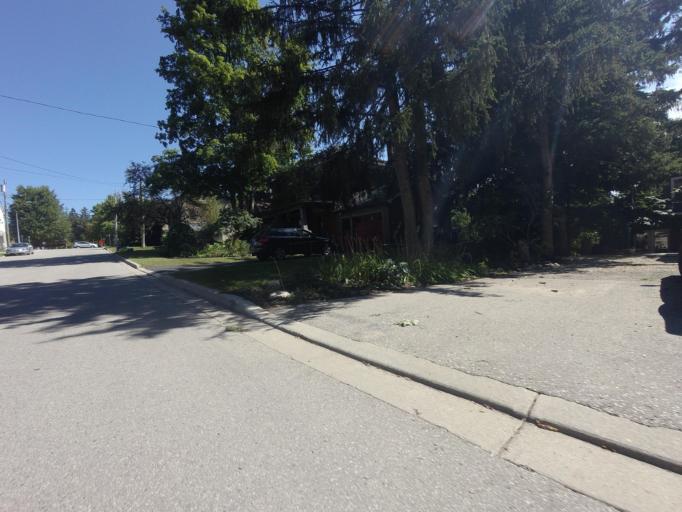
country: CA
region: Ontario
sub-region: Wellington County
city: Guelph
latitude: 43.7065
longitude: -80.3816
